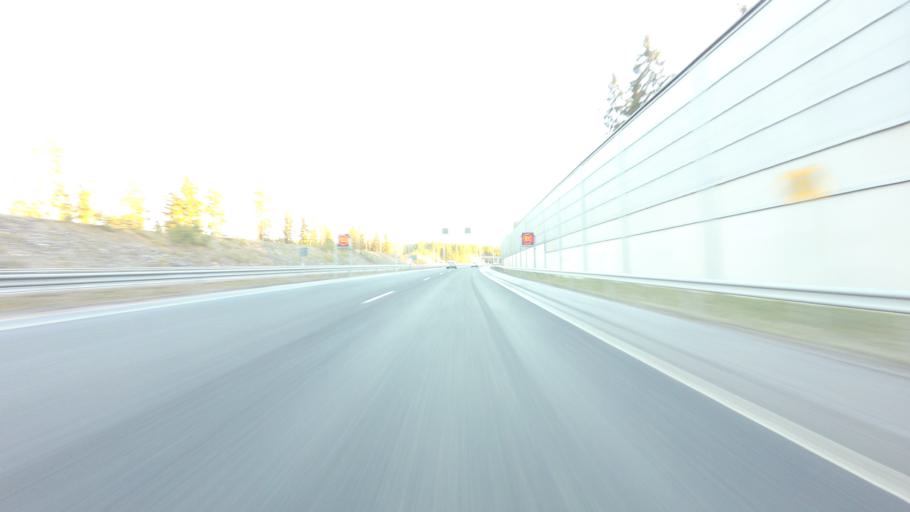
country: FI
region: Uusimaa
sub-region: Helsinki
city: Saukkola
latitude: 60.3233
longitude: 23.9577
